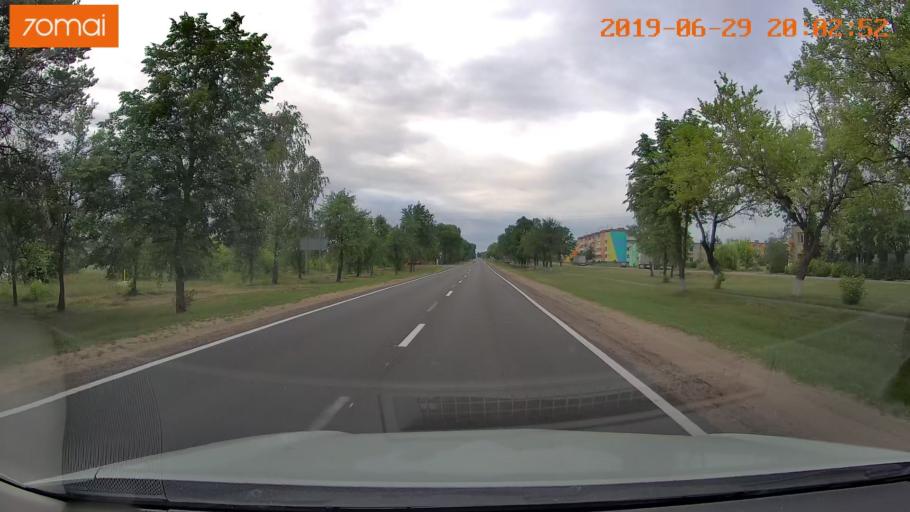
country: BY
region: Brest
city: Lahishyn
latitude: 52.3233
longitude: 25.9905
